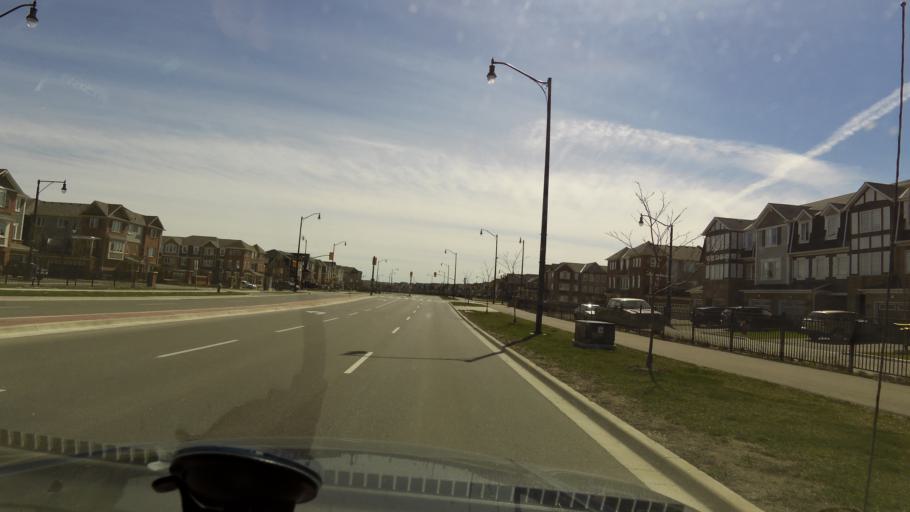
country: CA
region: Ontario
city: Brampton
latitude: 43.6802
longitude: -79.8280
